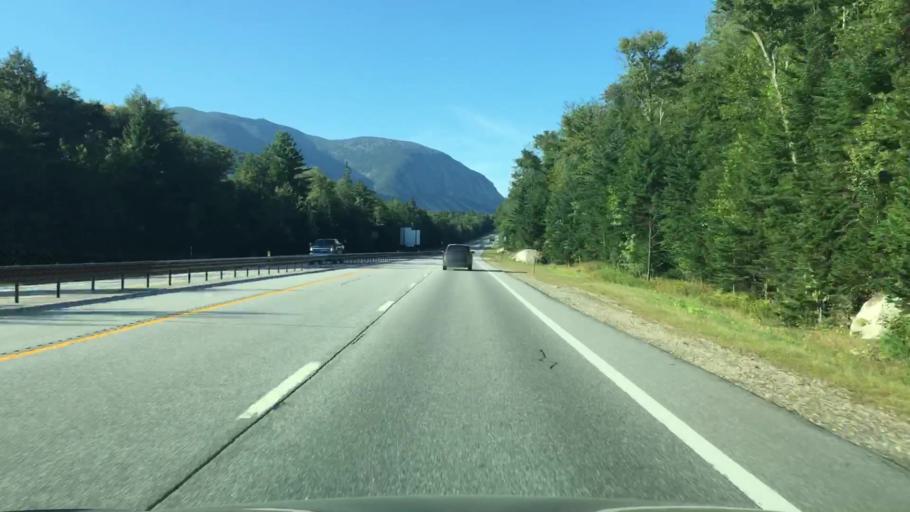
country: US
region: New Hampshire
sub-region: Grafton County
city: Deerfield
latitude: 44.1136
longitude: -71.6820
